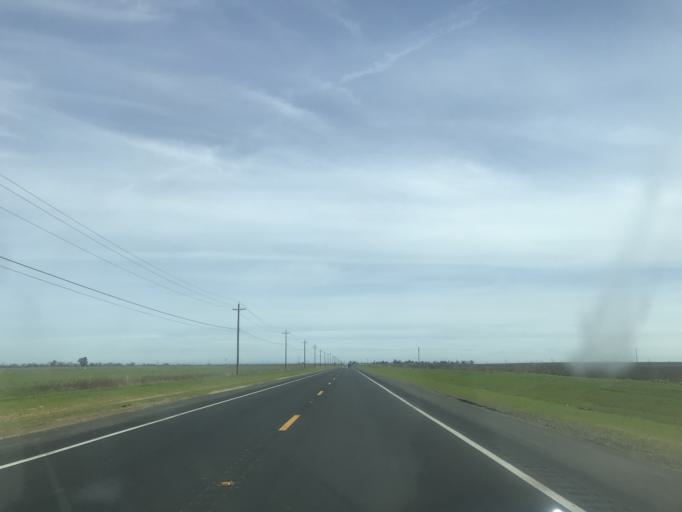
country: US
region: California
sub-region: Yolo County
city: Esparto
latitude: 38.6863
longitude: -121.9985
